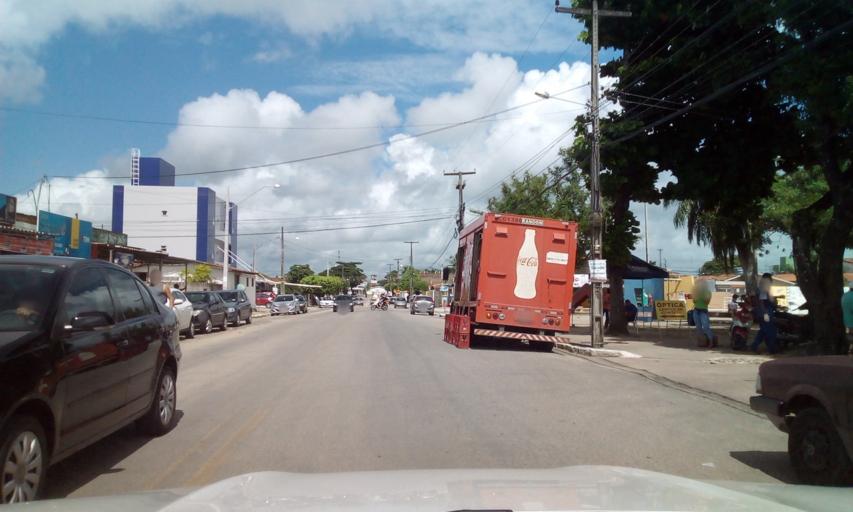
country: BR
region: Paraiba
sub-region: Joao Pessoa
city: Joao Pessoa
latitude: -7.1774
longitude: -34.8691
